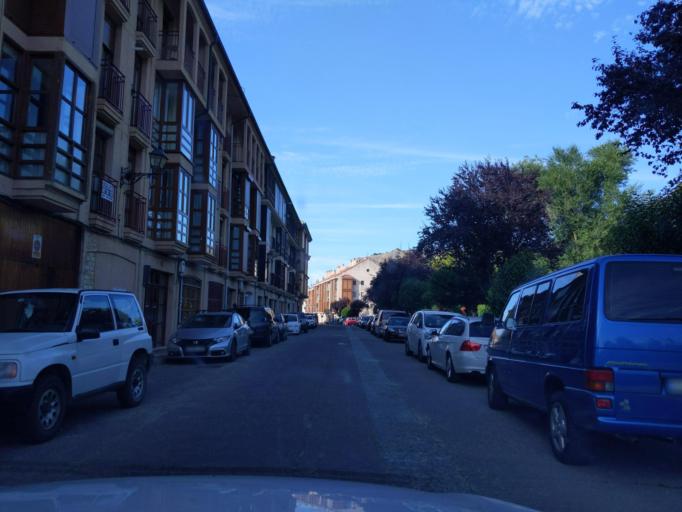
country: ES
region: La Rioja
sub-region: Provincia de La Rioja
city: Ezcaray
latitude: 42.3223
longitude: -3.0129
